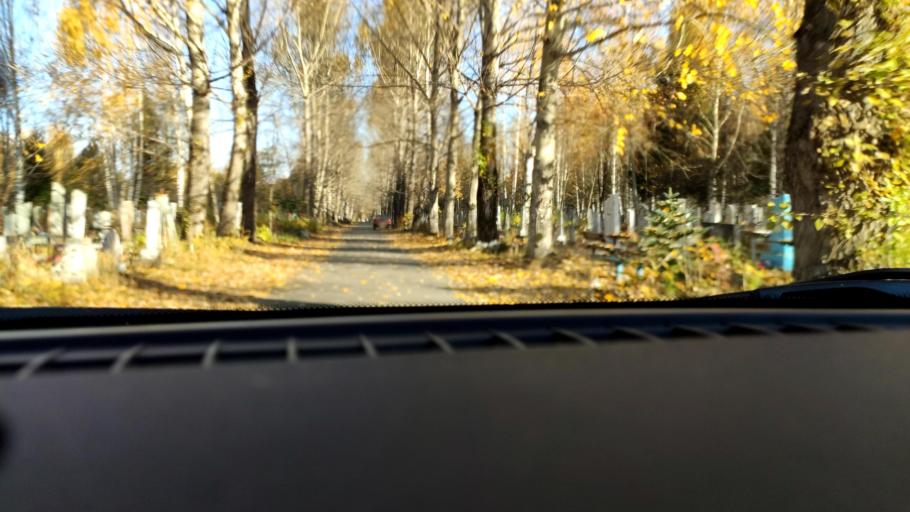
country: RU
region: Perm
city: Kondratovo
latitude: 58.0637
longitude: 56.1360
